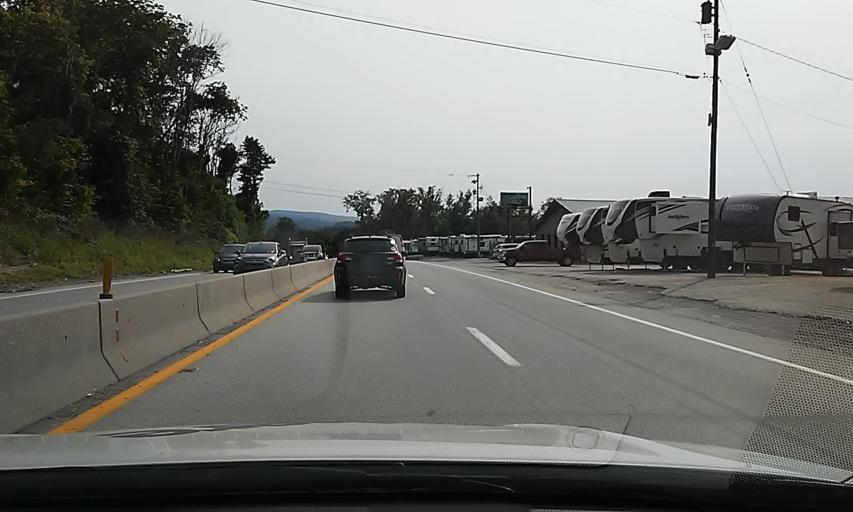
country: US
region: Pennsylvania
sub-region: Fayette County
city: Connellsville
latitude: 40.0326
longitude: -79.5872
